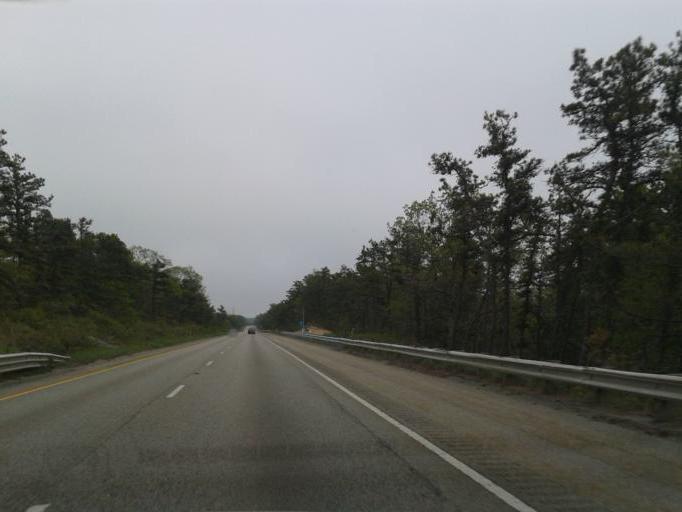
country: US
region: Massachusetts
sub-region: Plymouth County
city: White Island Shores
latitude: 41.8685
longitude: -70.5962
